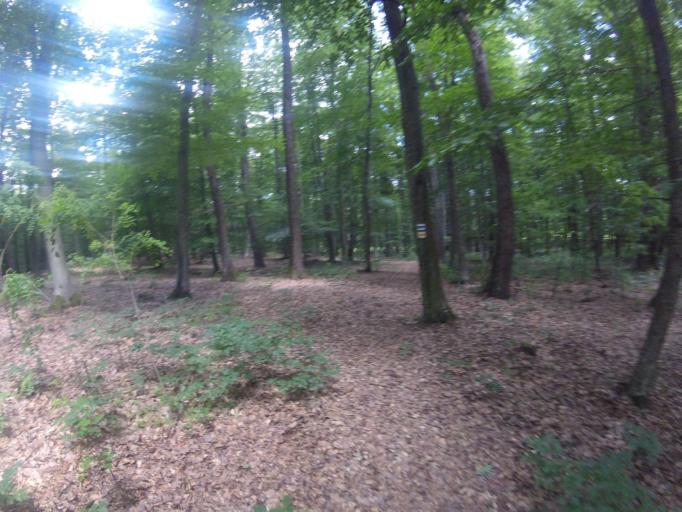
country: HU
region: Zala
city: Zalalovo
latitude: 46.8265
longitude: 16.5498
